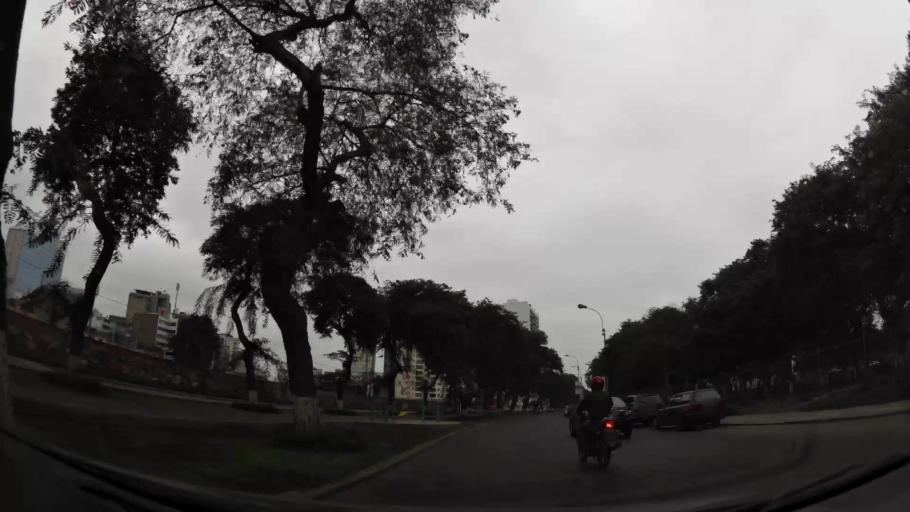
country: PE
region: Lima
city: Lima
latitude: -12.0681
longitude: -77.0396
